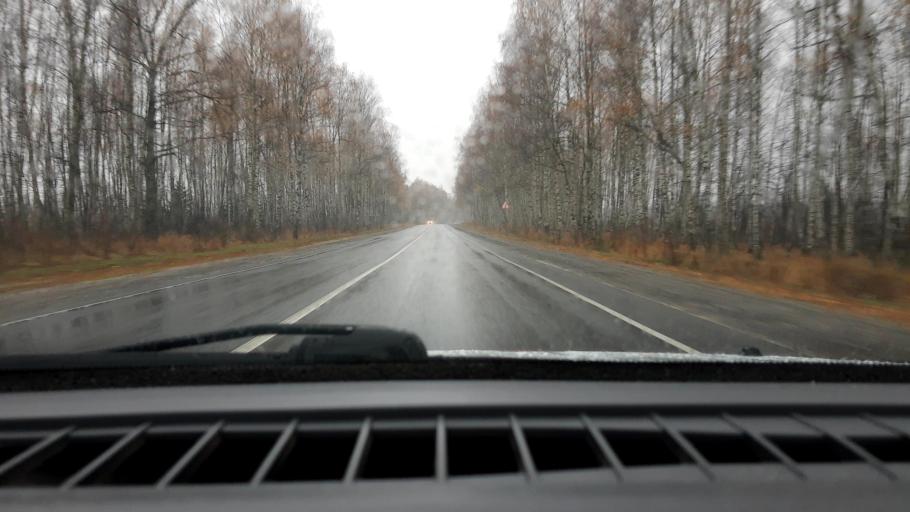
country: RU
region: Nizjnij Novgorod
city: Linda
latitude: 56.6743
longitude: 44.1438
